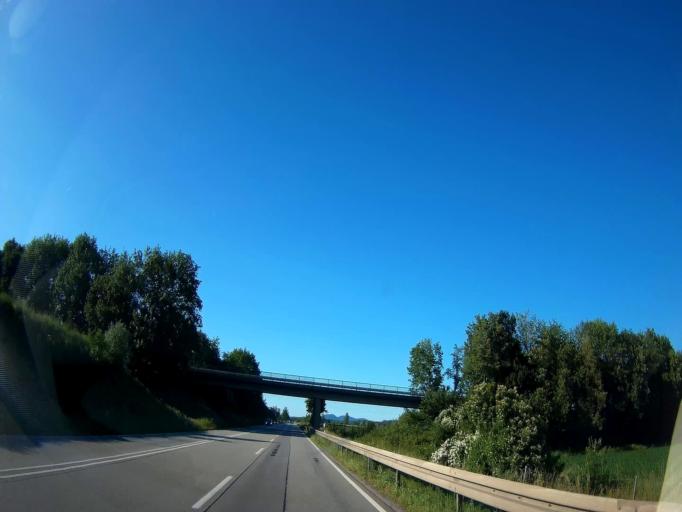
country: DE
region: Bavaria
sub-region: Lower Bavaria
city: Parkstetten
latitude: 48.9166
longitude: 12.6181
